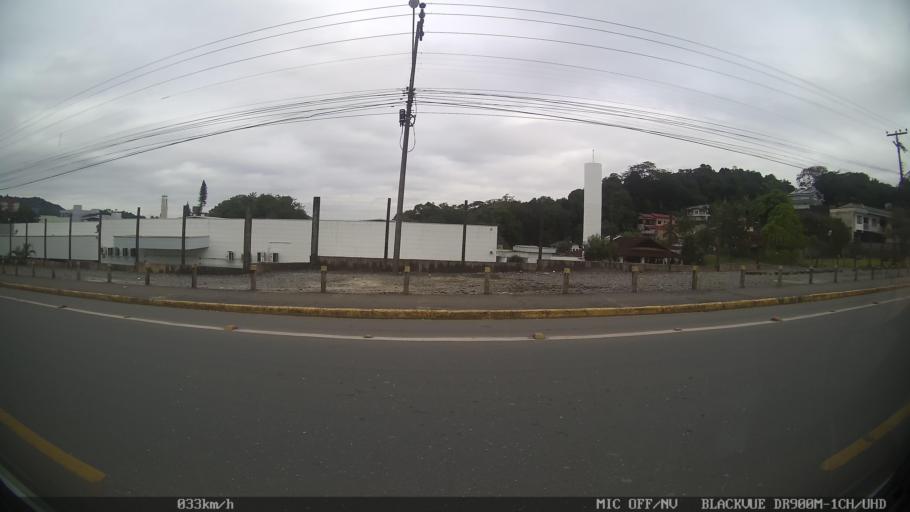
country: BR
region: Santa Catarina
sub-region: Joinville
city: Joinville
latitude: -26.2599
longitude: -48.8529
